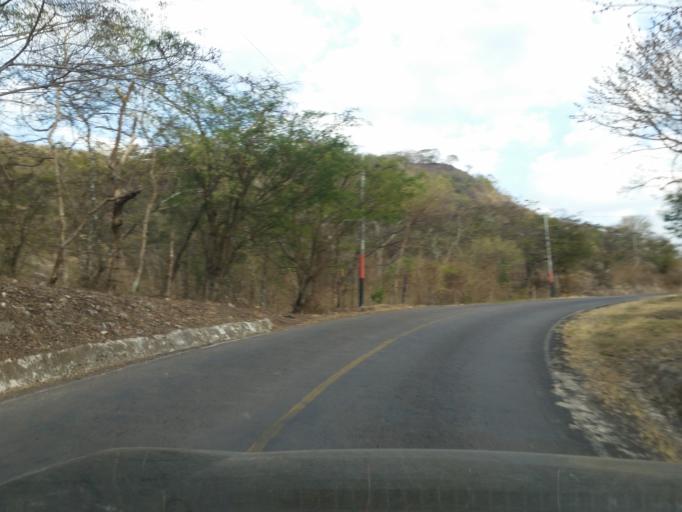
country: NI
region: Jinotega
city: San Rafael del Norte
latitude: 13.1964
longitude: -86.1339
